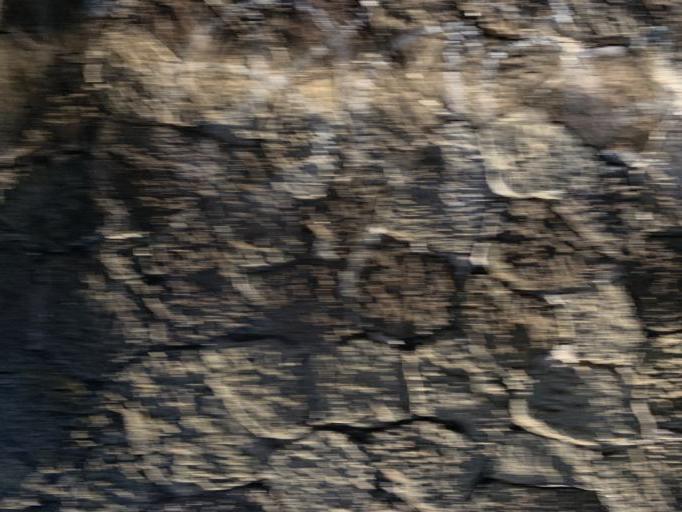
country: IT
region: Latium
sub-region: Citta metropolitana di Roma Capitale
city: Marino
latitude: 41.7847
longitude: 12.6488
